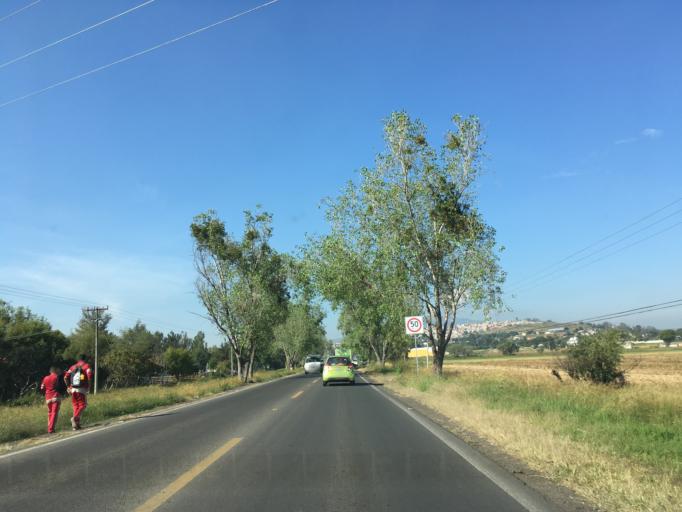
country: MX
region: Michoacan
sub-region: Tarimbaro
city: La Palma (Las Palmas)
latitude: 19.7715
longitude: -101.1473
